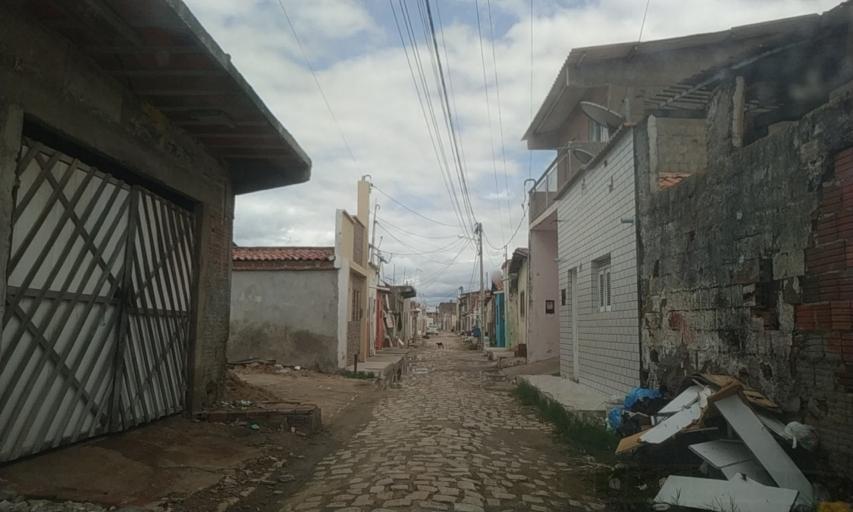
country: BR
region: Rio Grande do Norte
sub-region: Areia Branca
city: Areia Branca
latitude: -4.9555
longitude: -37.1297
